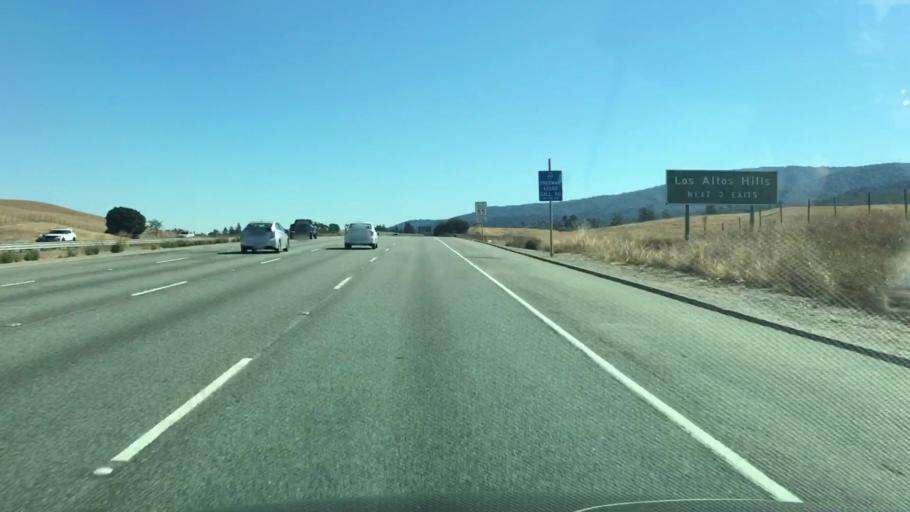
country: US
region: California
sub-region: San Mateo County
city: Ladera
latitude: 37.3976
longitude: -122.1805
